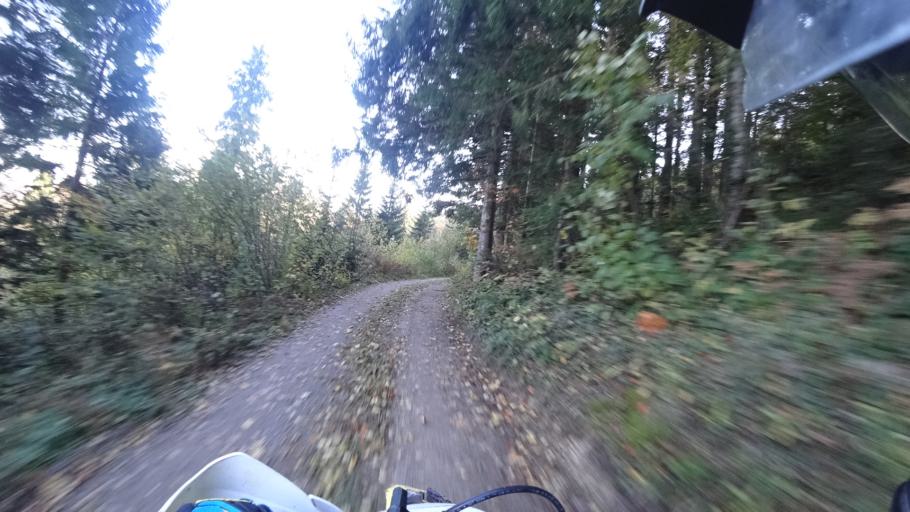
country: HR
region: Karlovacka
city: Plaski
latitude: 44.9968
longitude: 15.4095
